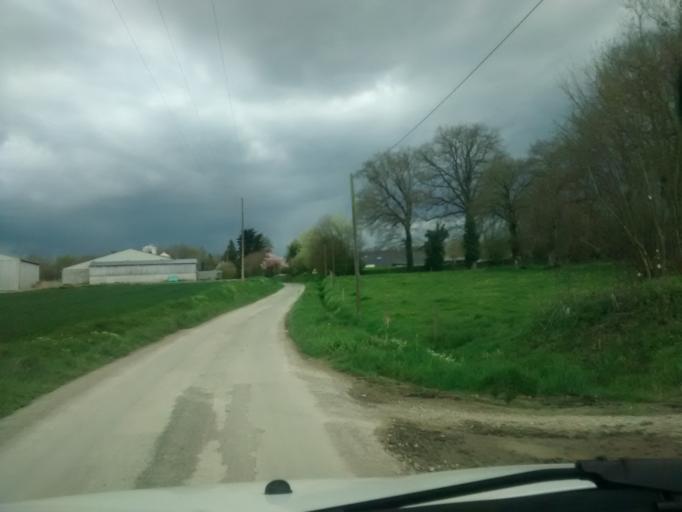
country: FR
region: Brittany
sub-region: Departement d'Ille-et-Vilaine
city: Brece
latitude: 48.1448
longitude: -1.4945
